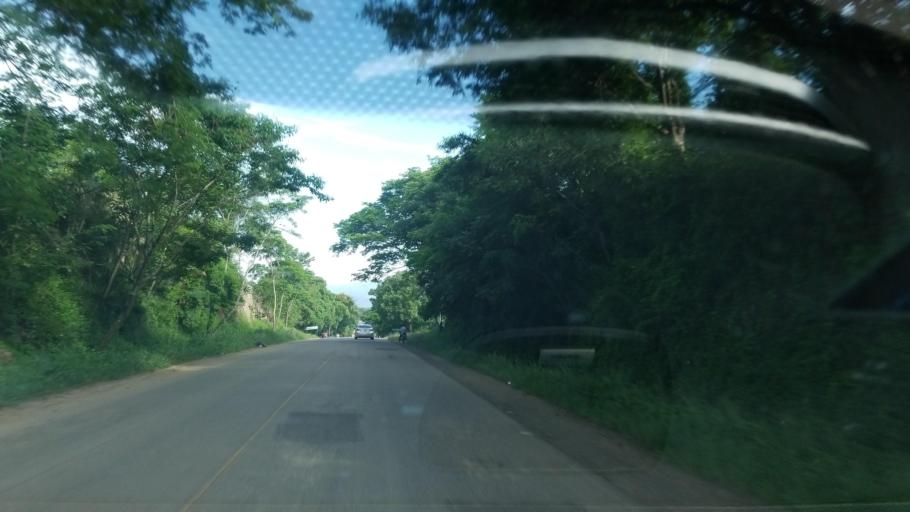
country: HN
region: El Paraiso
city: Arauli
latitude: 13.9479
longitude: -86.5600
